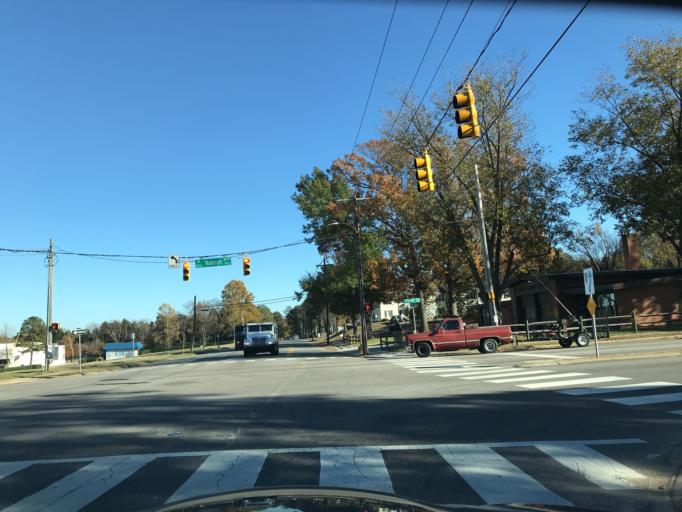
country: US
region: North Carolina
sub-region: Wake County
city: Raleigh
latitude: 35.7929
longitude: -78.6133
